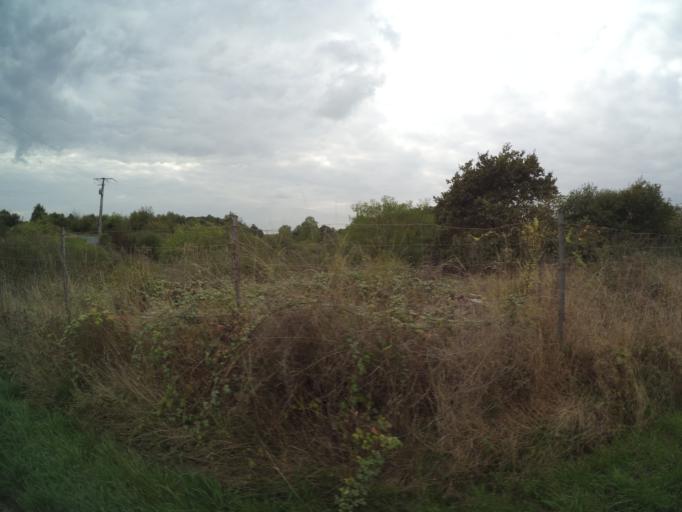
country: FR
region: Centre
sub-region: Departement d'Indre-et-Loire
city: Poce-sur-Cisse
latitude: 47.4982
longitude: 0.9814
